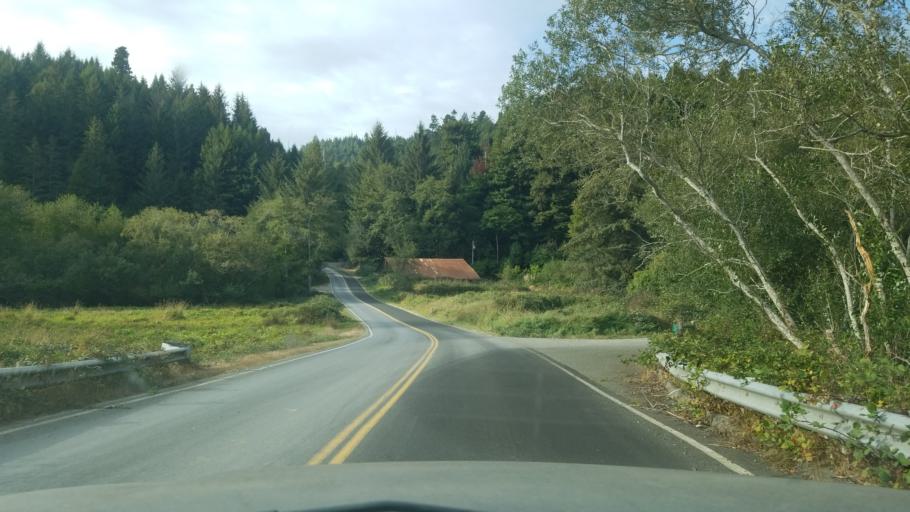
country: US
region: California
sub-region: Humboldt County
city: Westhaven-Moonstone
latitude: 41.3222
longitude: -124.0428
